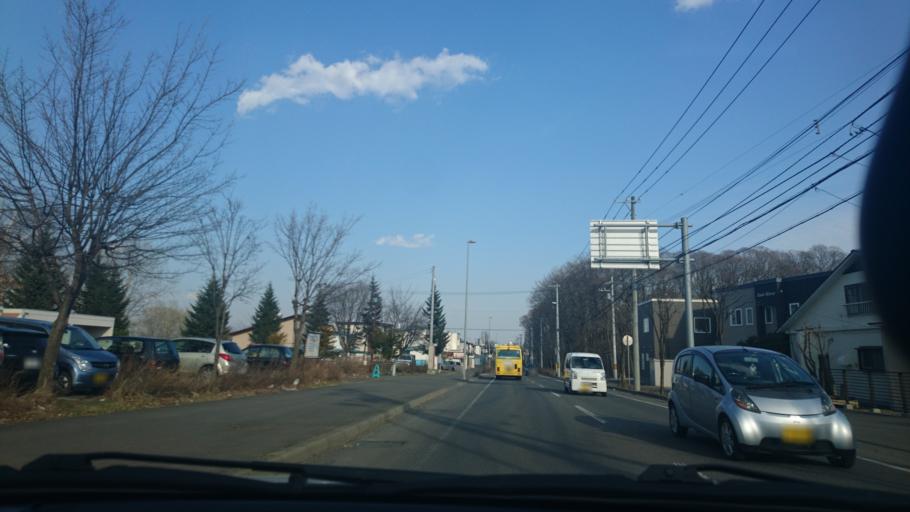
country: JP
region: Hokkaido
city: Obihiro
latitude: 42.9246
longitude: 143.1723
